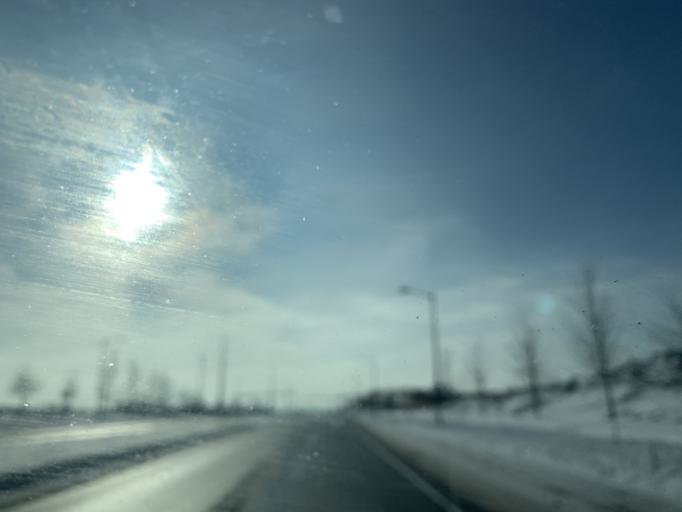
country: US
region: Minnesota
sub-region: Dakota County
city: Apple Valley
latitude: 44.6968
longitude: -93.2176
